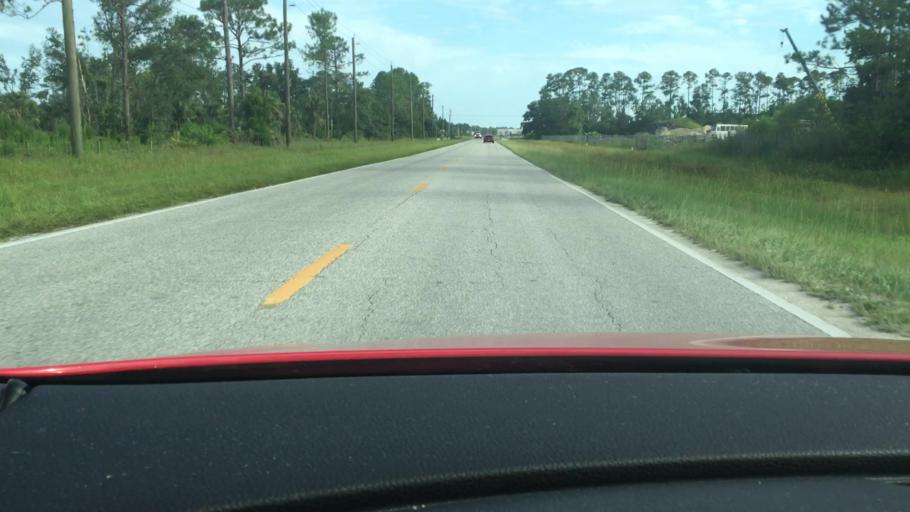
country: US
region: Florida
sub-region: Volusia County
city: Daytona Beach
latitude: 29.1811
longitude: -81.0920
